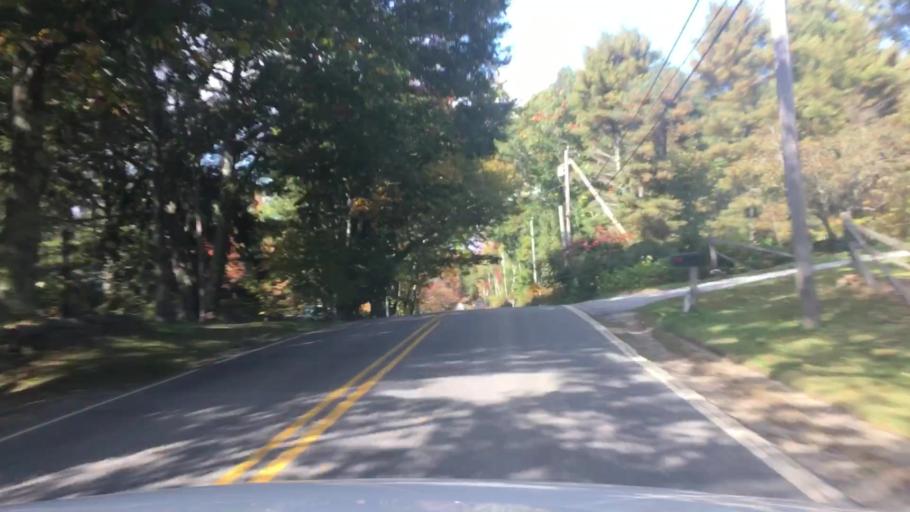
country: US
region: Maine
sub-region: Knox County
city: Warren
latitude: 44.1505
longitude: -69.2387
